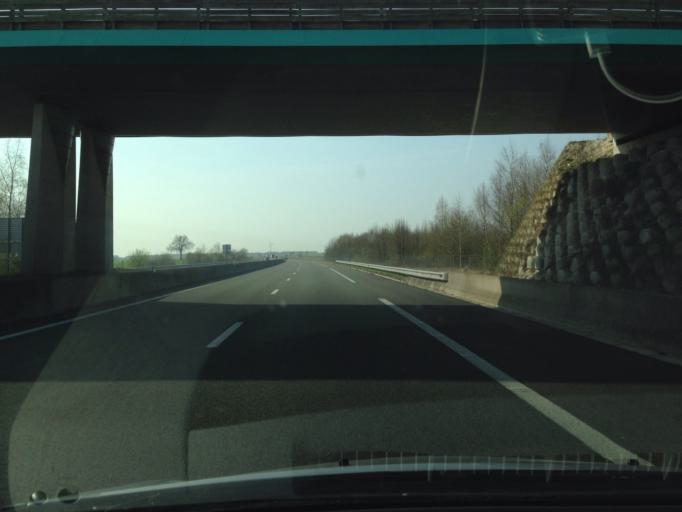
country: FR
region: Picardie
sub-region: Departement de la Somme
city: Sailly-Flibeaucourt
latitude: 50.1576
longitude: 1.7849
